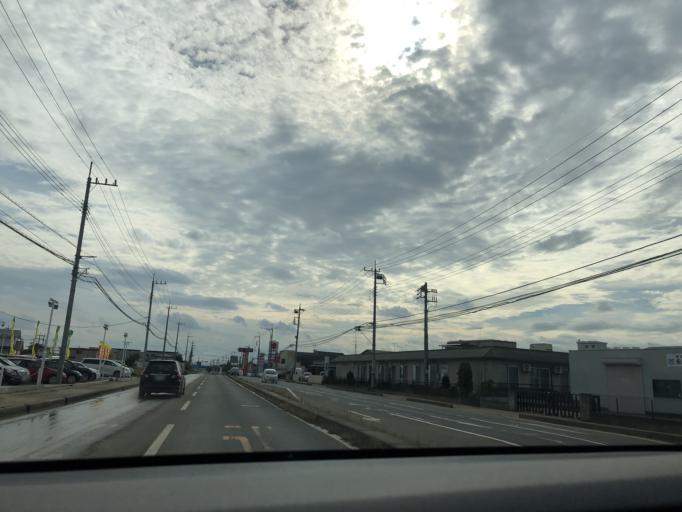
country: JP
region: Tochigi
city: Sano
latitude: 36.2947
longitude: 139.5664
